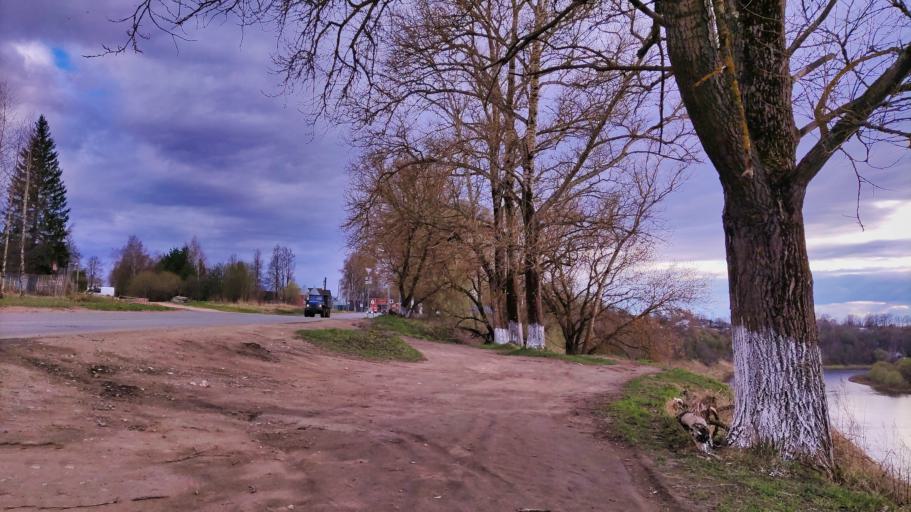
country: RU
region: Tverskaya
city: Rzhev
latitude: 56.2535
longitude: 34.3140
